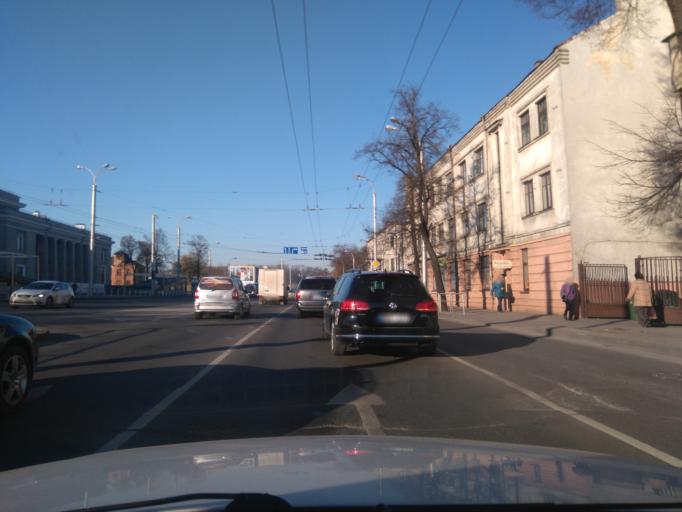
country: LT
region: Kauno apskritis
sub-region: Kaunas
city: Aleksotas
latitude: 54.8873
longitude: 23.9317
